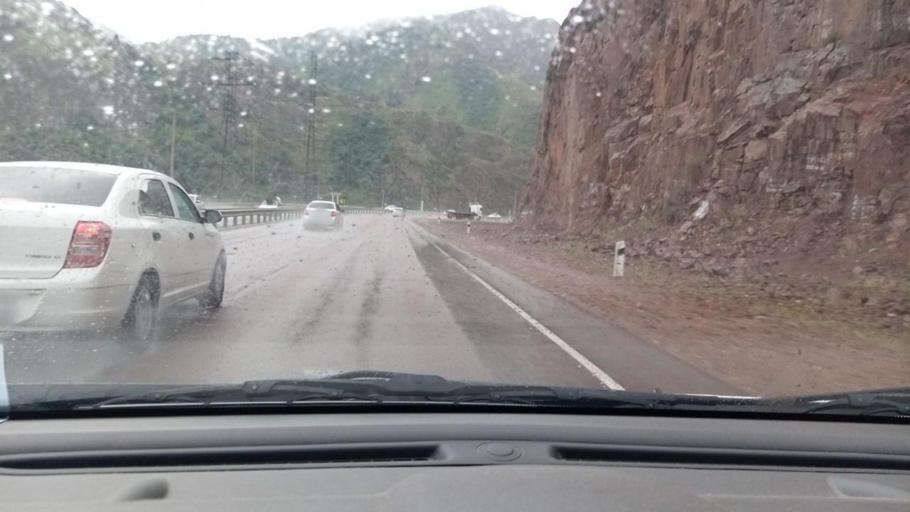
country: UZ
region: Toshkent
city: Angren
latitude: 41.0753
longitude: 70.3128
